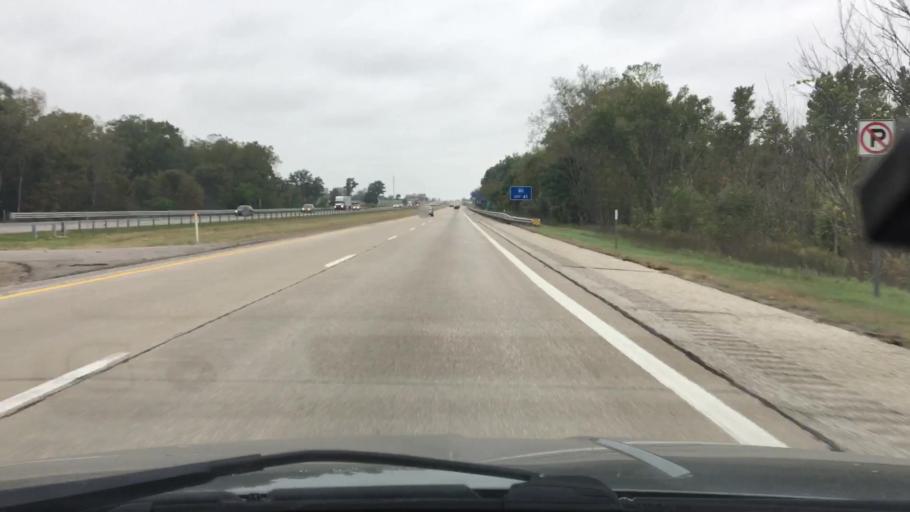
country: US
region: Michigan
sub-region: Berrien County
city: Watervliet
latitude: 42.1792
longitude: -86.2478
